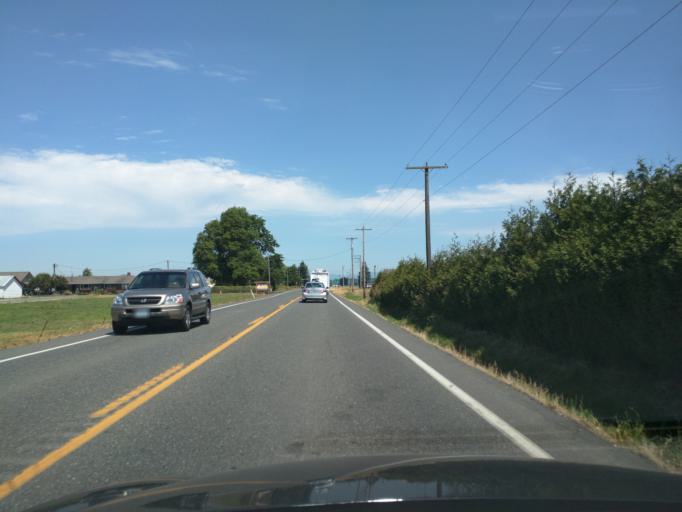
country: US
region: Washington
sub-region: Whatcom County
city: Lynden
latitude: 48.9606
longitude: -122.4852
